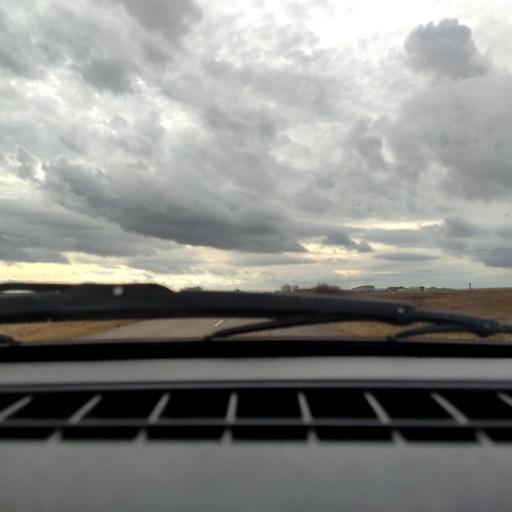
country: RU
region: Bashkortostan
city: Asanovo
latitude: 54.9186
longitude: 55.5078
